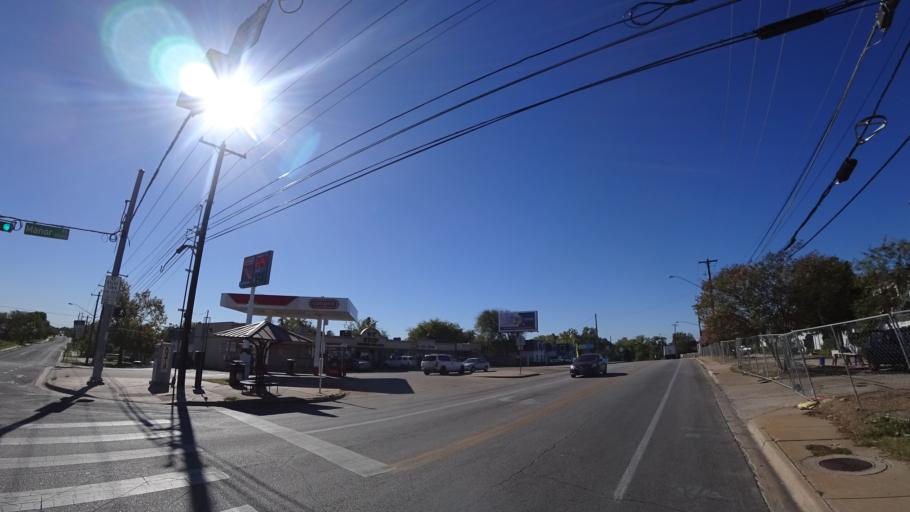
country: US
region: Texas
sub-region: Travis County
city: Austin
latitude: 30.2981
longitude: -97.6871
